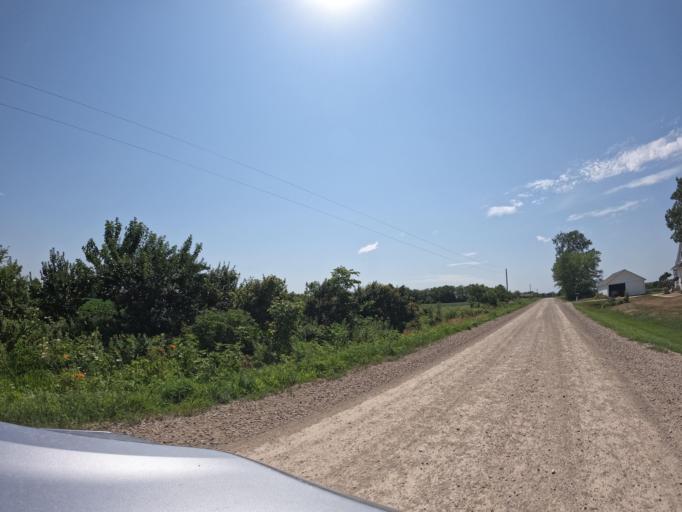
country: US
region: Iowa
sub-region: Henry County
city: Mount Pleasant
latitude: 40.8900
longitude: -91.6437
